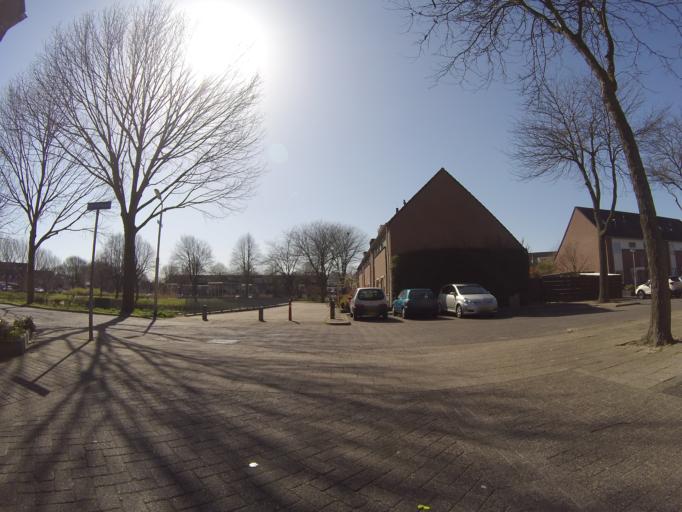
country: NL
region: Utrecht
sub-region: Gemeente Amersfoort
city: Hoogland
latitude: 52.1783
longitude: 5.3727
